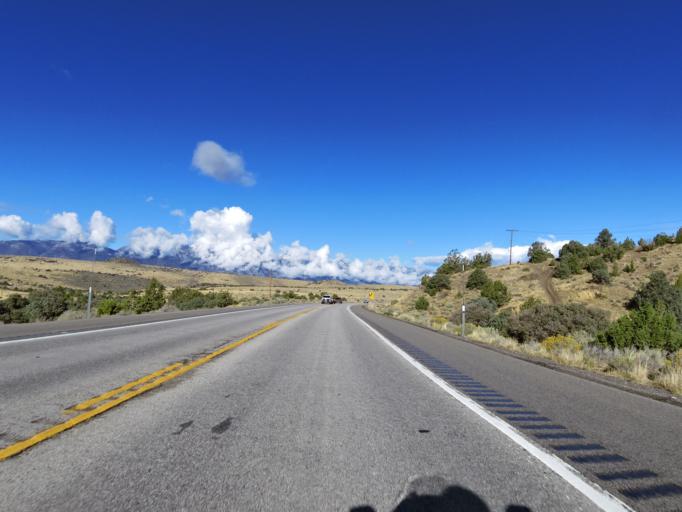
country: US
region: Nevada
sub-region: Douglas County
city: Gardnerville Ranchos
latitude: 38.8533
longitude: -119.6574
